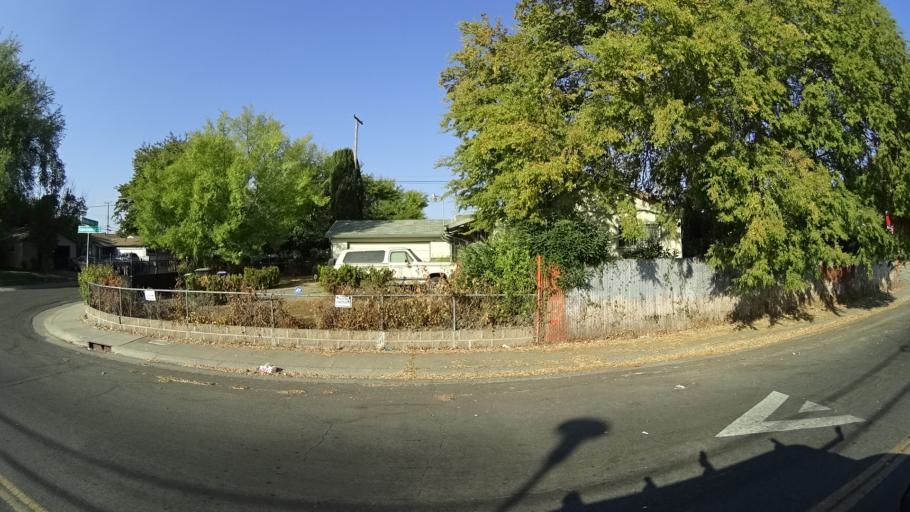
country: US
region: California
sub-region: Sacramento County
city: Parkway
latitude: 38.4890
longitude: -121.4876
